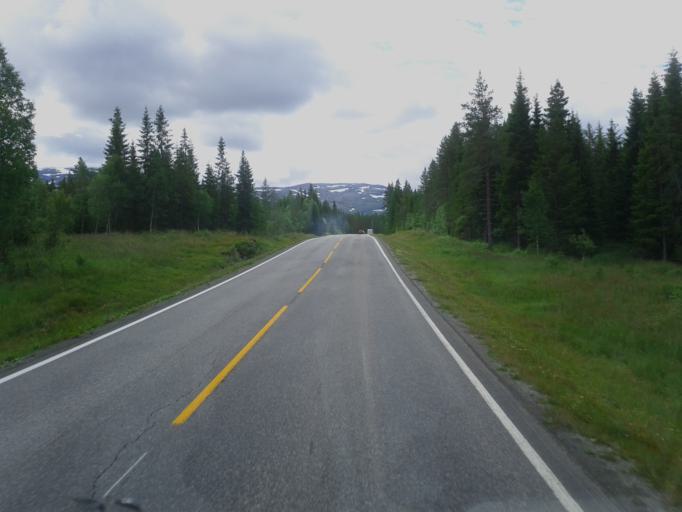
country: NO
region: Nord-Trondelag
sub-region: Hoylandet
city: Hoylandet
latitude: 64.6582
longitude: 12.6485
